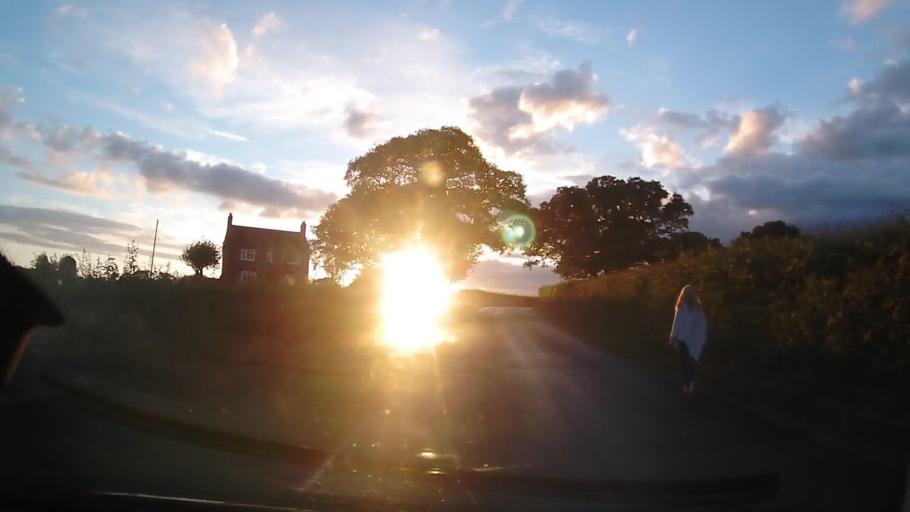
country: GB
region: England
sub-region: Shropshire
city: Prees
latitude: 52.9031
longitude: -2.6917
